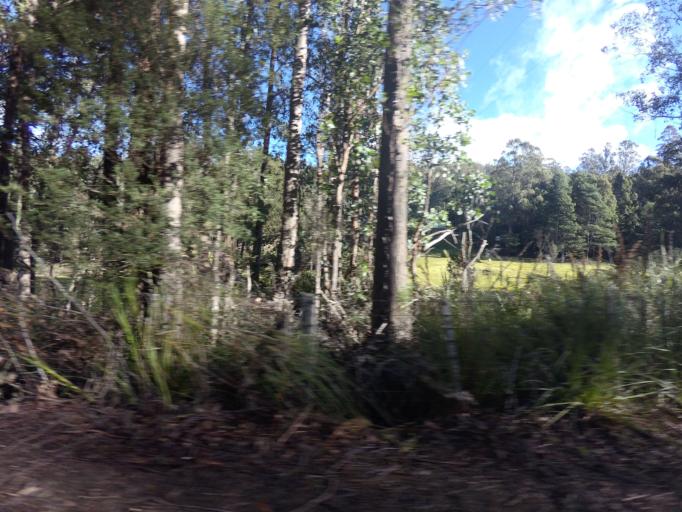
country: AU
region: Tasmania
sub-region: Glenorchy
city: Berriedale
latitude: -42.8470
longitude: 147.1671
